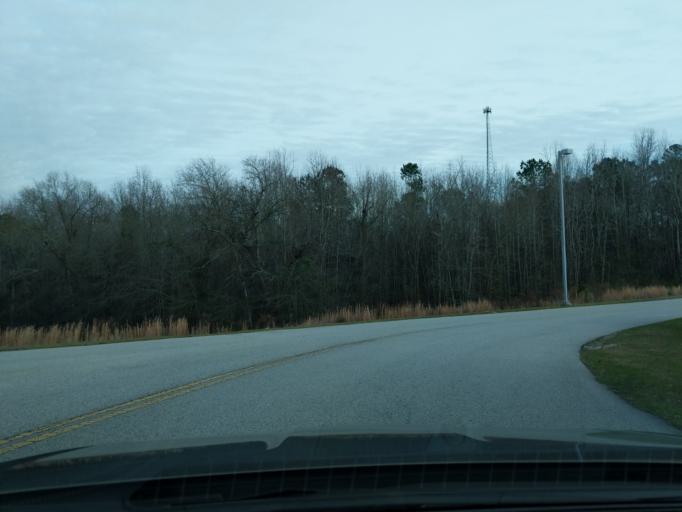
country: US
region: Georgia
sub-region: Columbia County
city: Grovetown
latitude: 33.4651
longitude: -82.1951
